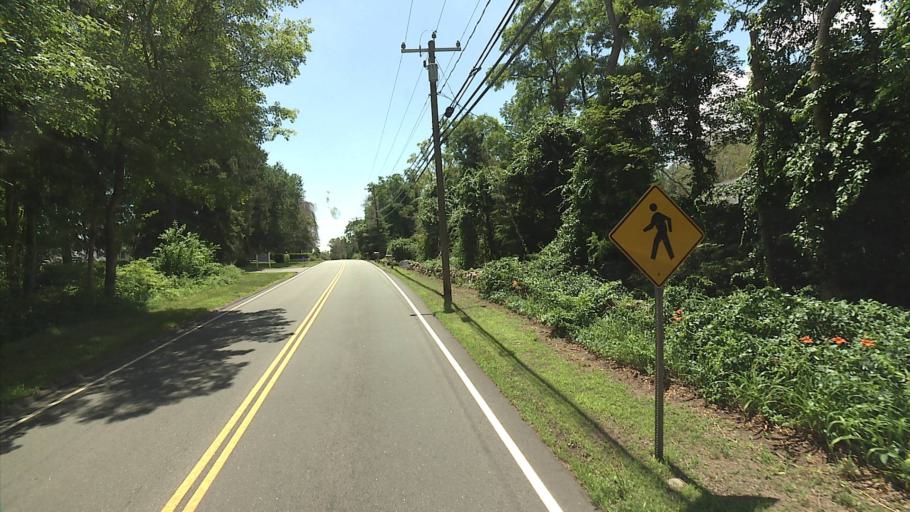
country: US
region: Connecticut
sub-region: Middlesex County
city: Moodus
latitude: 41.4866
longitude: -72.4470
